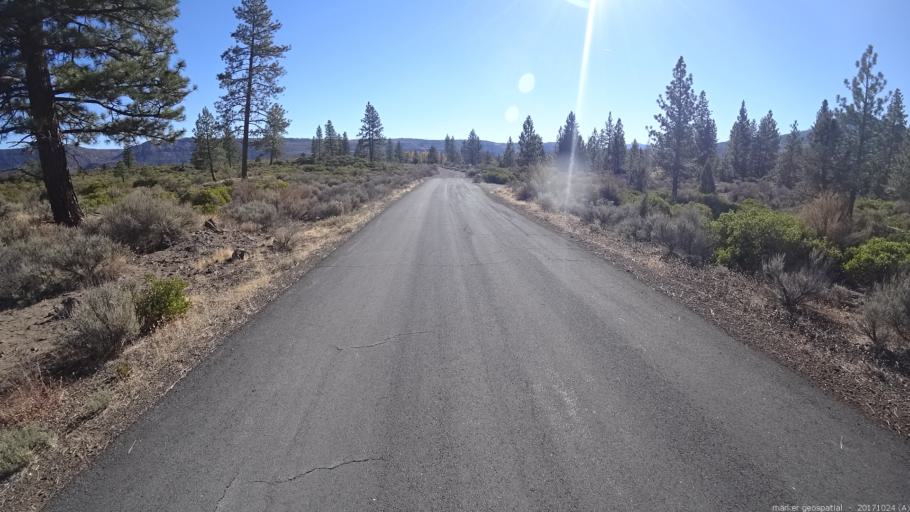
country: US
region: California
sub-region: Shasta County
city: Burney
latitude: 40.7510
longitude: -121.4589
